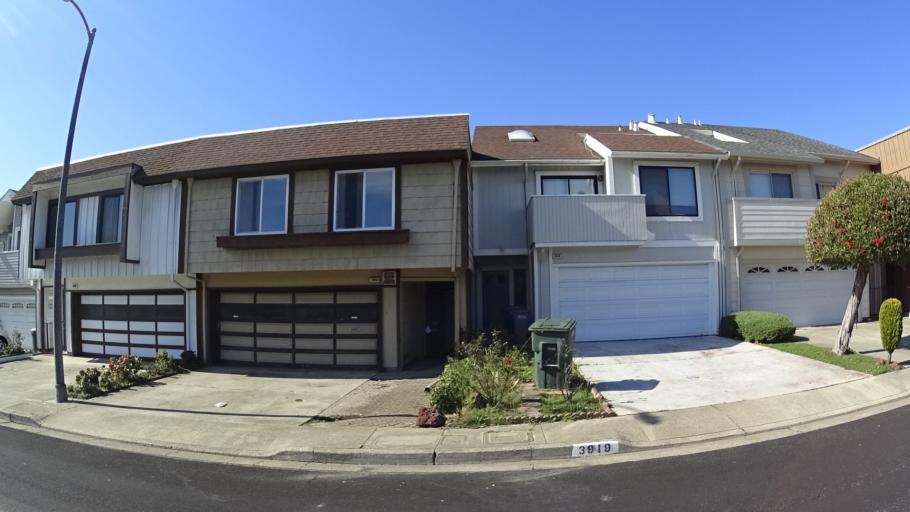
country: US
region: California
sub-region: San Mateo County
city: Colma
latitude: 37.6492
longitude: -122.4620
